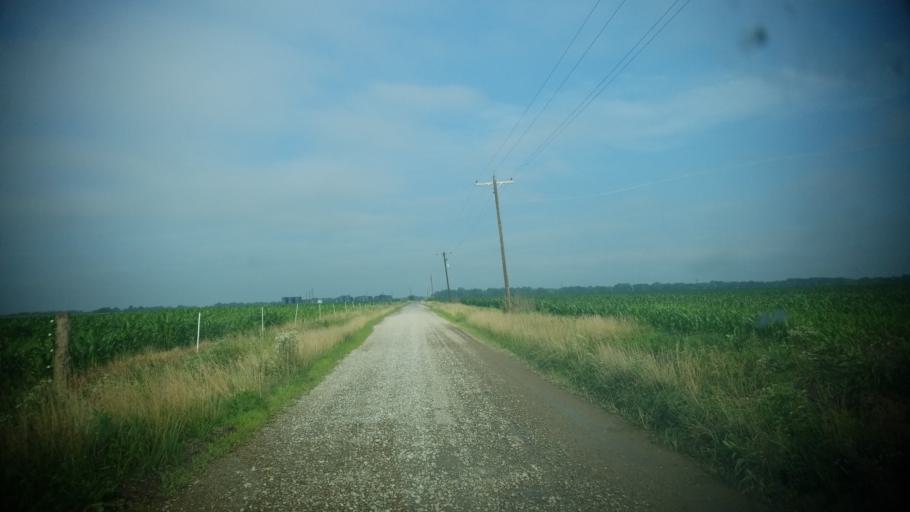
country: US
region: Illinois
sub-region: Clay County
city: Flora
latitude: 38.6016
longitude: -88.3447
